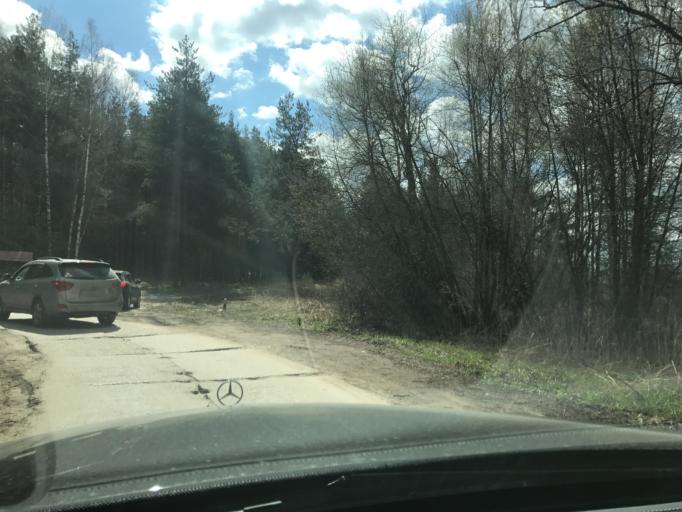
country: RU
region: Moskovskaya
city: Vereya
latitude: 55.8384
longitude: 39.0843
